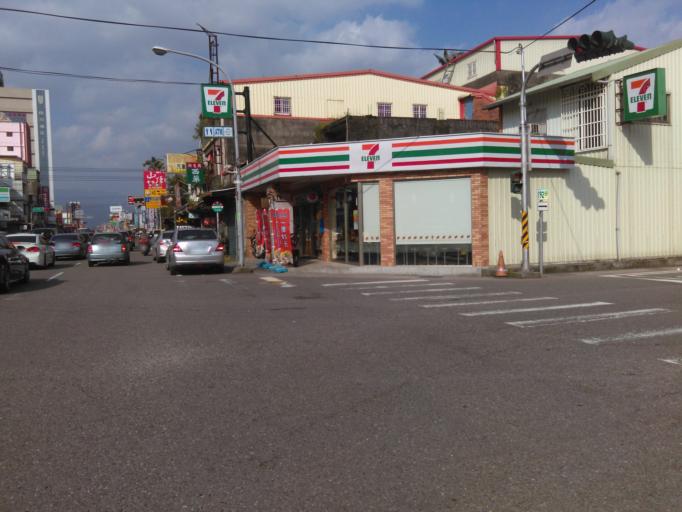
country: TW
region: Taiwan
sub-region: Yilan
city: Yilan
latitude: 24.7680
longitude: 121.7562
